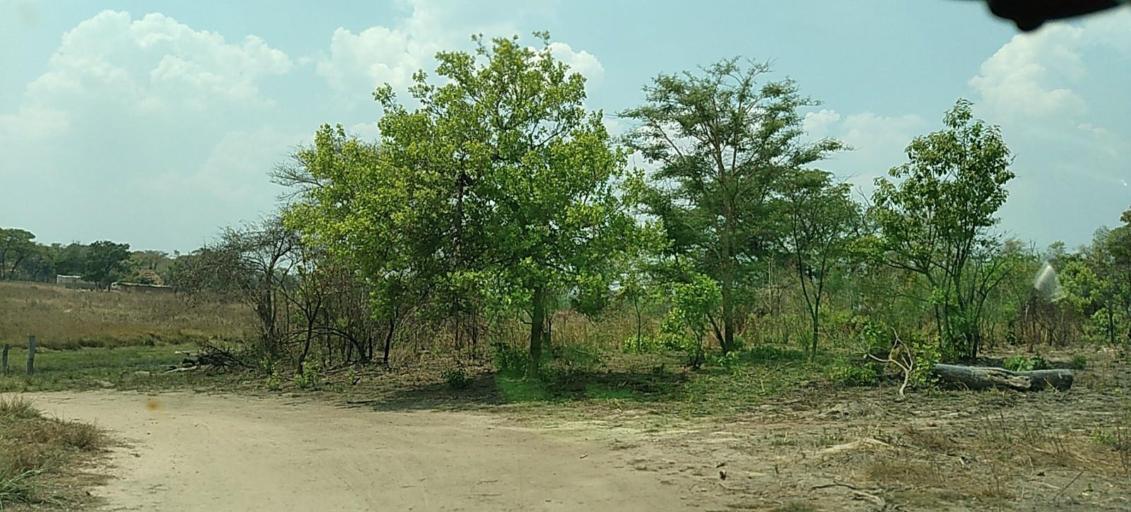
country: ZM
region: North-Western
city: Kabompo
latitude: -13.6348
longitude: 24.3853
